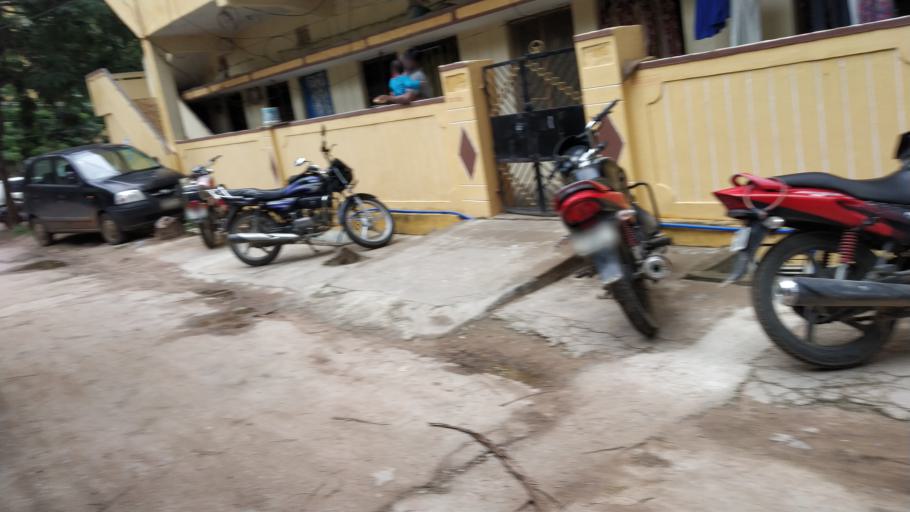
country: IN
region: Telangana
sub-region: Medak
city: Serilingampalle
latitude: 17.5095
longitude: 78.3050
